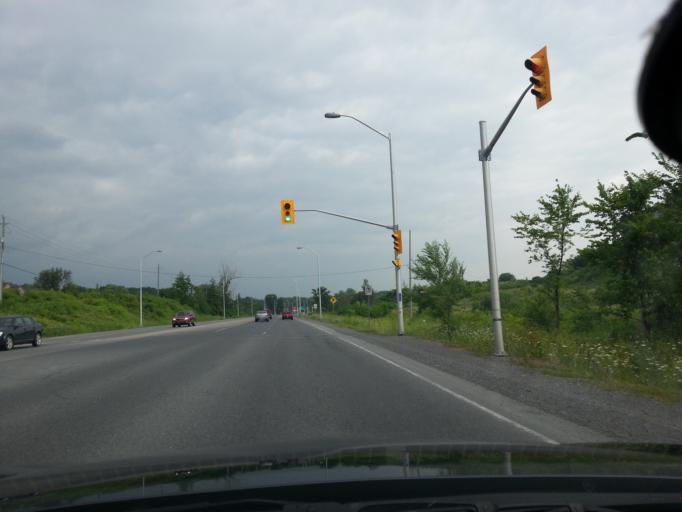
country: CA
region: Ontario
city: Clarence-Rockland
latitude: 45.5477
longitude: -75.3003
